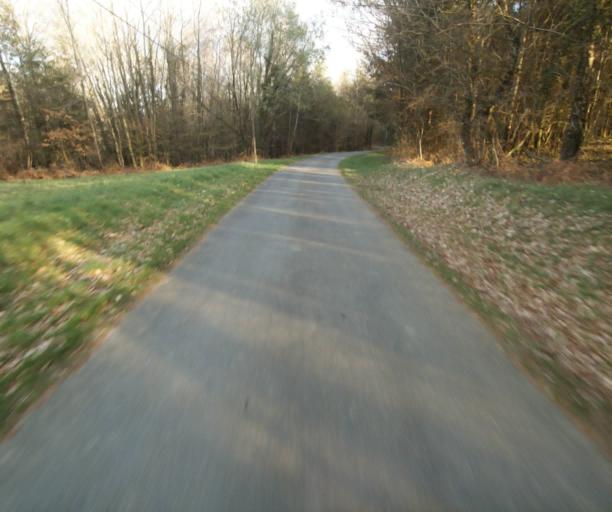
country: FR
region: Limousin
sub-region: Departement de la Correze
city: Uzerche
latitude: 45.3674
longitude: 1.5885
